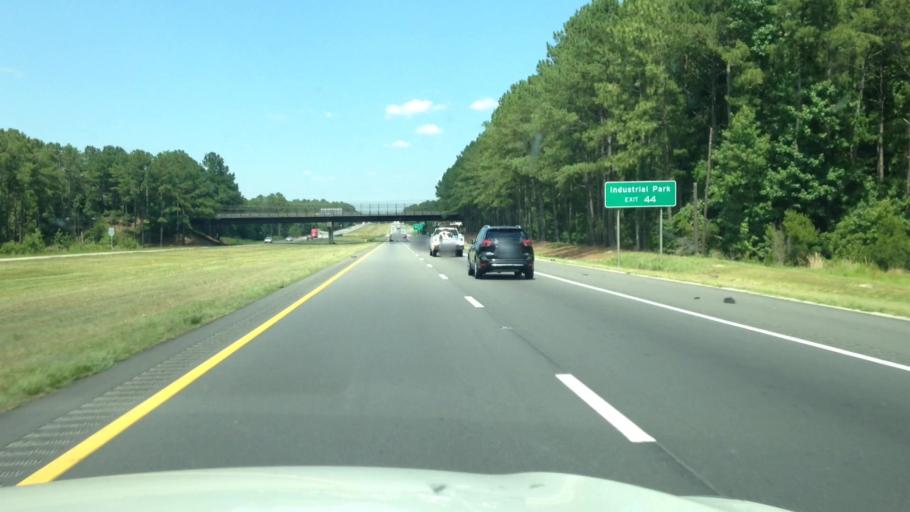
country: US
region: North Carolina
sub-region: Cumberland County
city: Hope Mills
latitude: 34.9550
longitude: -78.8973
